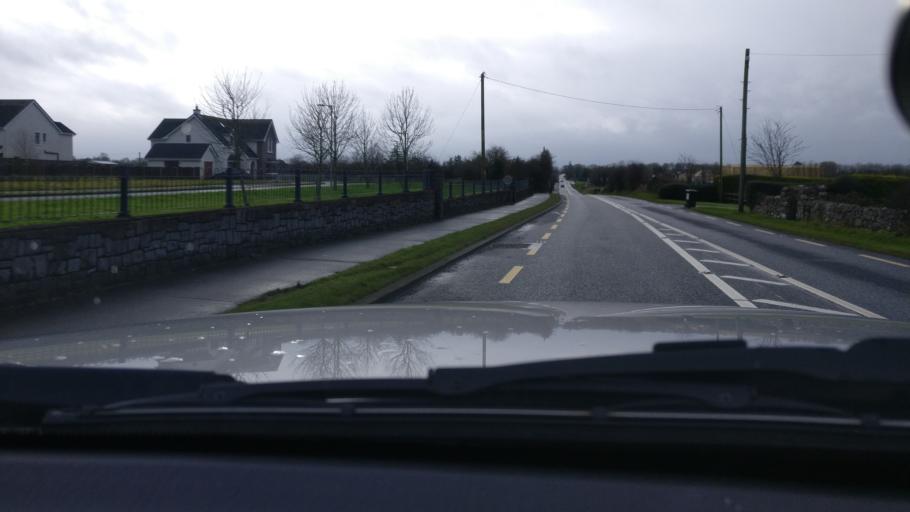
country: IE
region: Leinster
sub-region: An Longfort
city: Ballymahon
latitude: 53.5562
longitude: -7.7684
